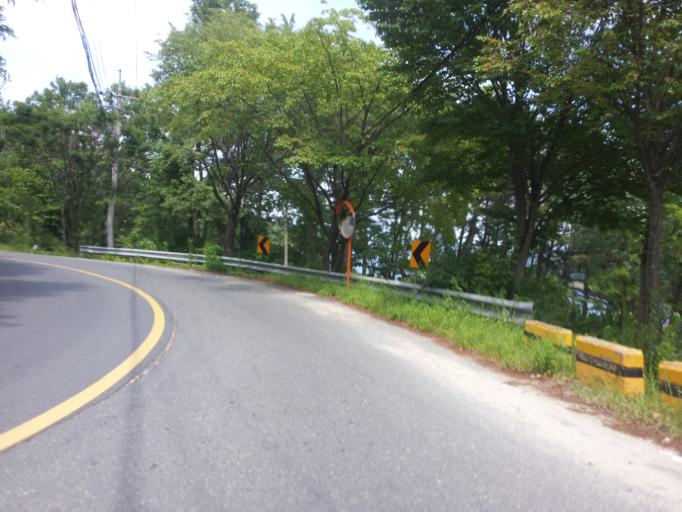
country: KR
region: Daejeon
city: Sintansin
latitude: 36.4288
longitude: 127.4675
